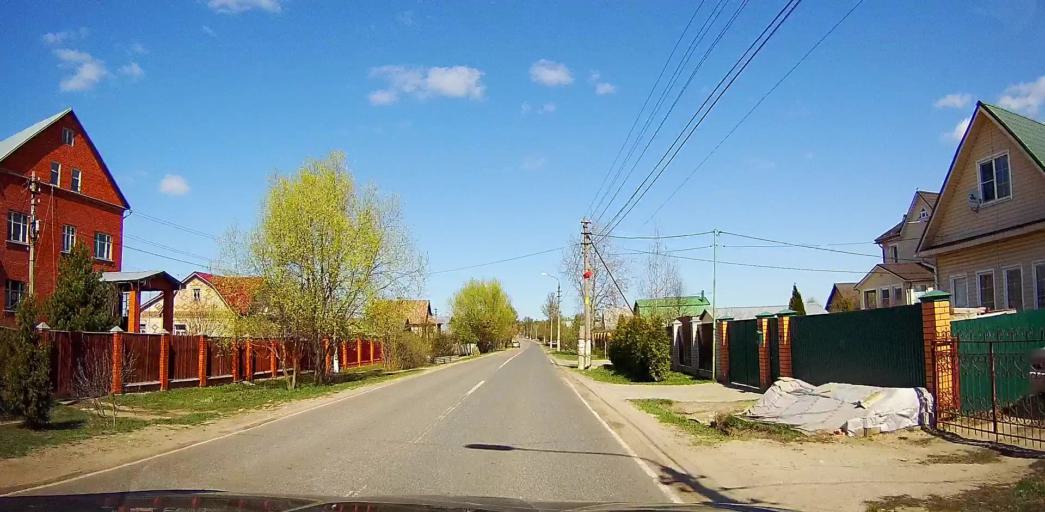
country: RU
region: Moskovskaya
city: Ramenskoye
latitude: 55.6186
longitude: 38.3029
